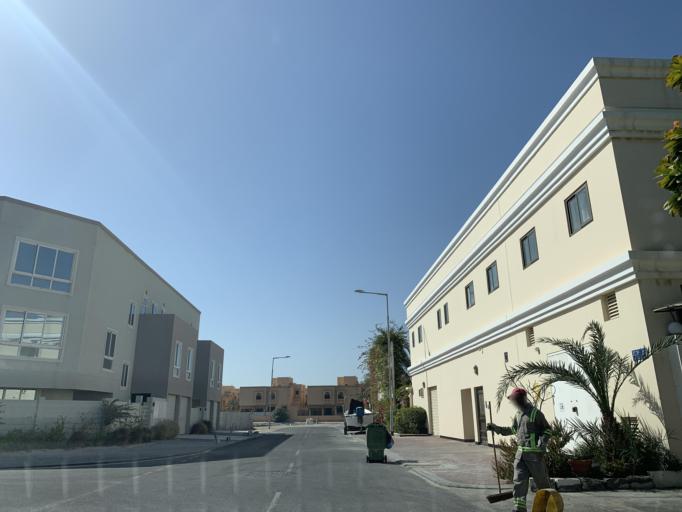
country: BH
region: Manama
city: Manama
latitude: 26.2025
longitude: 50.5713
